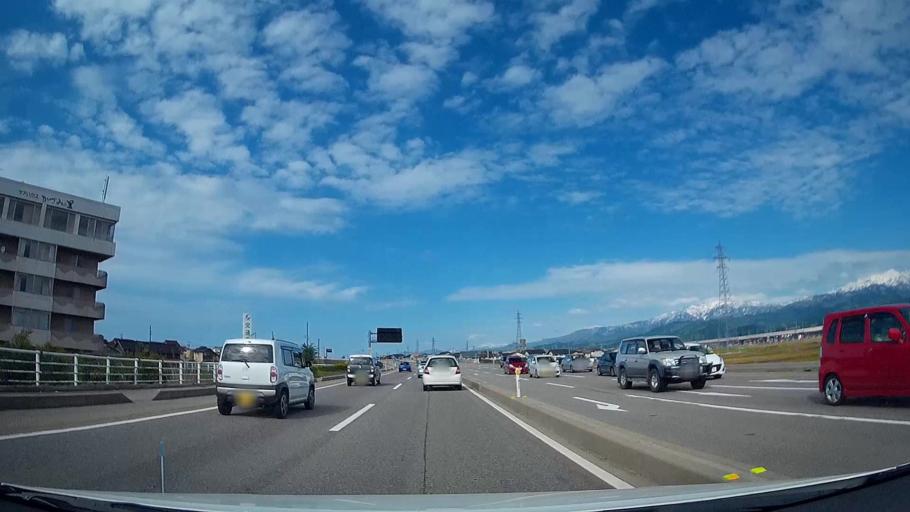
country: JP
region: Toyama
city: Namerikawa
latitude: 36.7511
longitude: 137.3539
